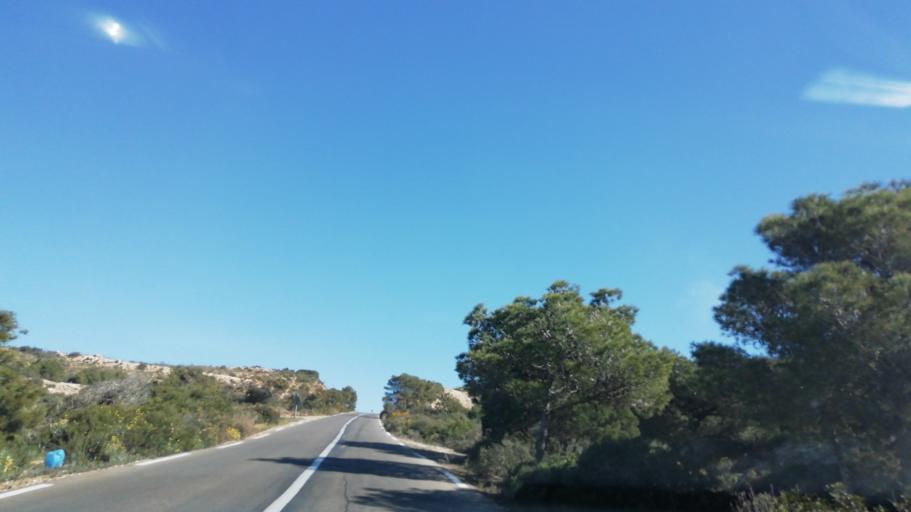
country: DZ
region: Ain Temouchent
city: El Amria
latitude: 35.6517
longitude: -1.0390
